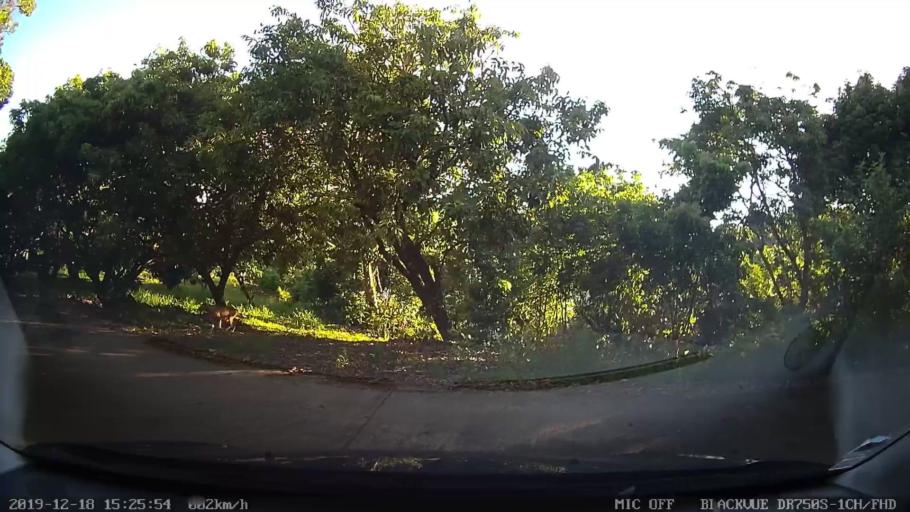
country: RE
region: Reunion
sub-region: Reunion
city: Bras-Panon
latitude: -21.0029
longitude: 55.6521
